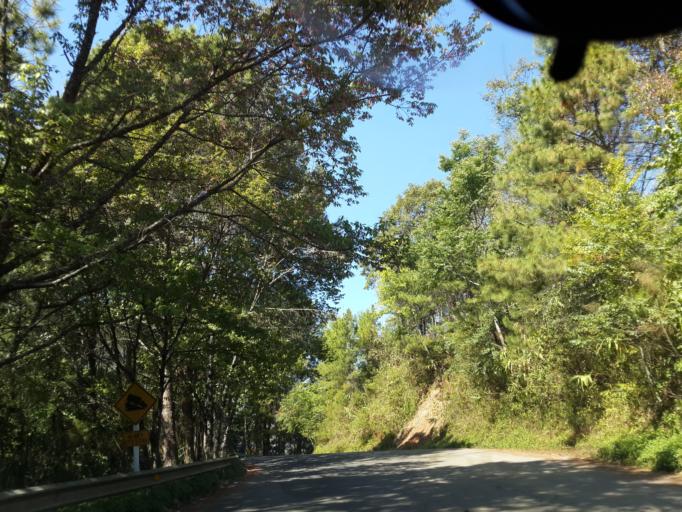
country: TH
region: Chiang Mai
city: Fang
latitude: 19.8975
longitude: 99.0456
